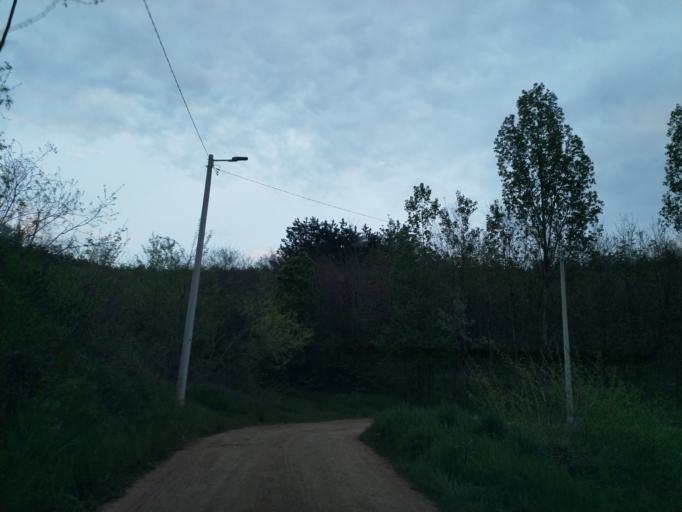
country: RS
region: Central Serbia
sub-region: Pomoravski Okrug
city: Paracin
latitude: 43.9423
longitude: 21.5117
